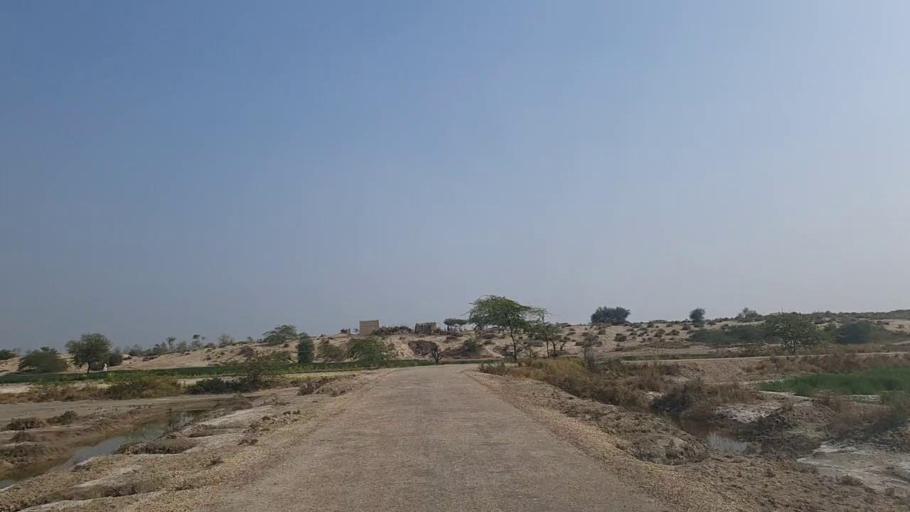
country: PK
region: Sindh
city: Daur
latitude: 26.4671
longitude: 68.4555
